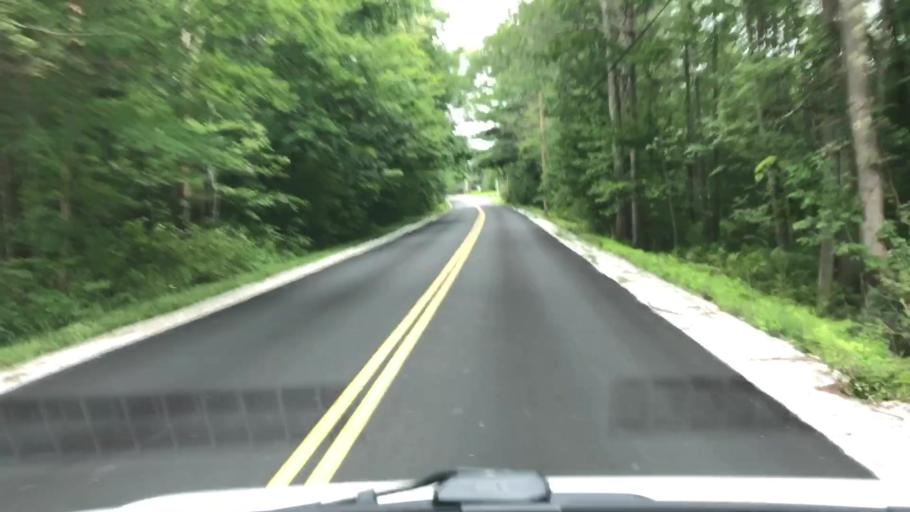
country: US
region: Massachusetts
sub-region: Berkshire County
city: Stockbridge
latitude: 42.2900
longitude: -73.2865
